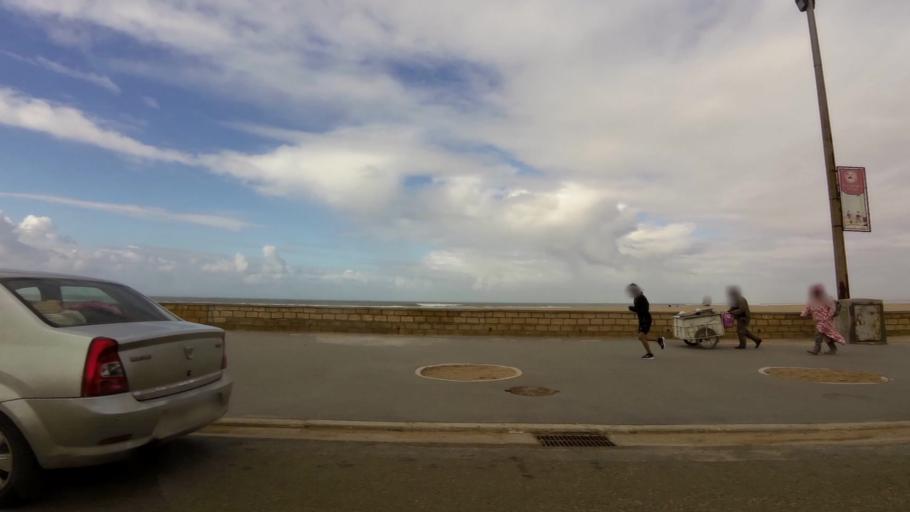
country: MA
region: Doukkala-Abda
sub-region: El-Jadida
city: El Jadida
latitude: 33.2443
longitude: -8.4880
